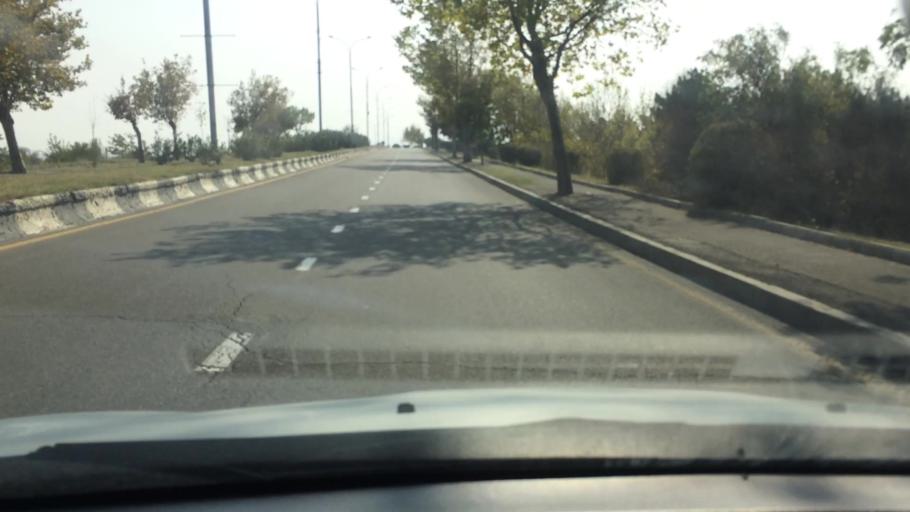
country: GE
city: Didi Lilo
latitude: 41.6883
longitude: 44.9530
